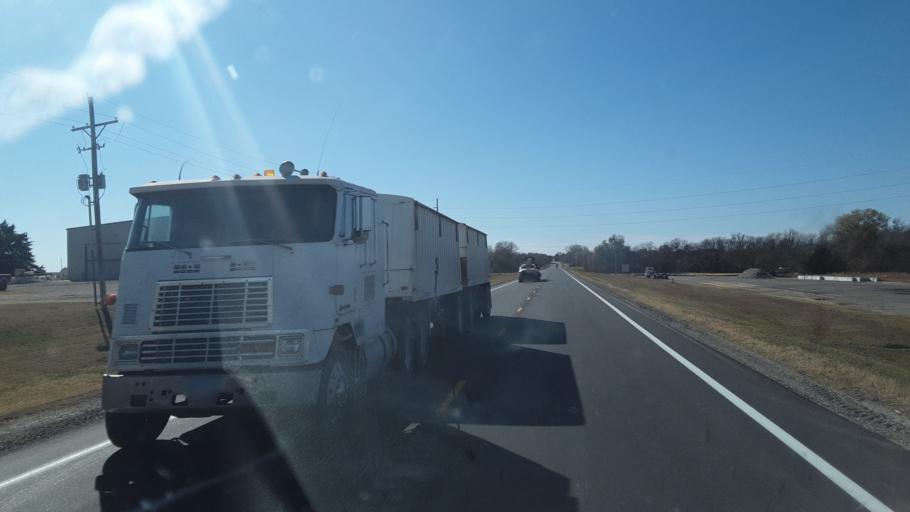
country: US
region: Kansas
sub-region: Rice County
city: Lyons
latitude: 38.3573
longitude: -98.1751
